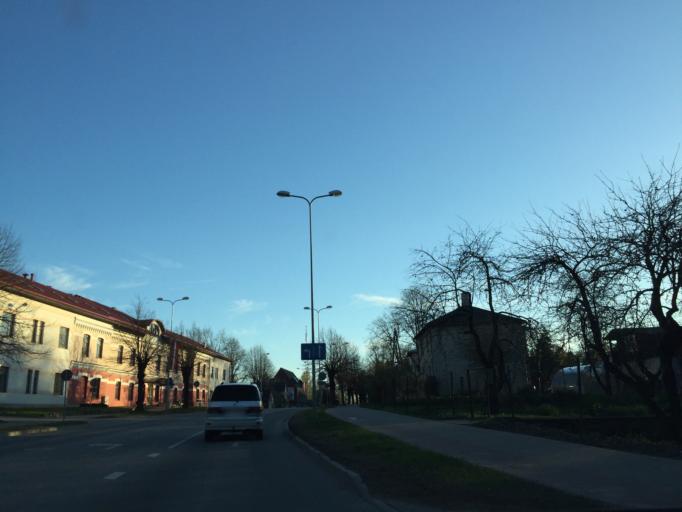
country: LV
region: Valmieras Rajons
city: Valmiera
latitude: 57.5352
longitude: 25.4040
